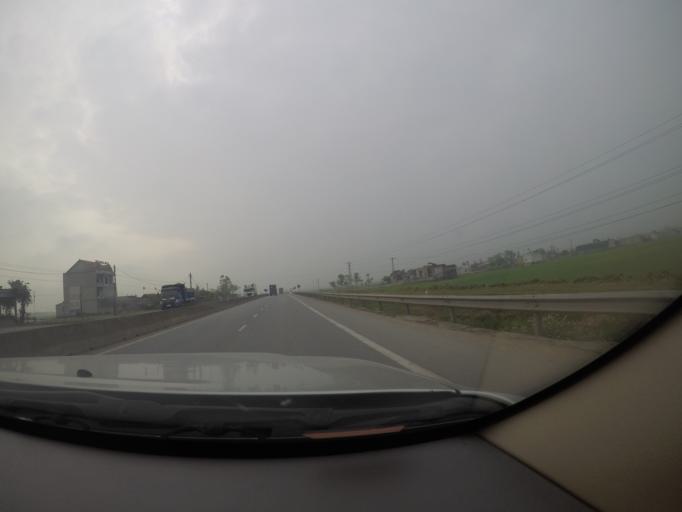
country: VN
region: Ha Tinh
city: Ky Anh
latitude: 18.1846
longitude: 106.1962
